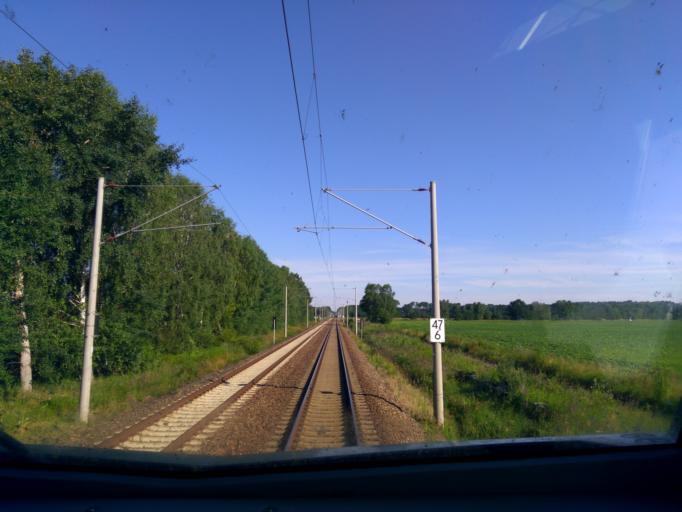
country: DE
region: Brandenburg
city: Halbe
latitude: 52.1302
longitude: 13.6788
